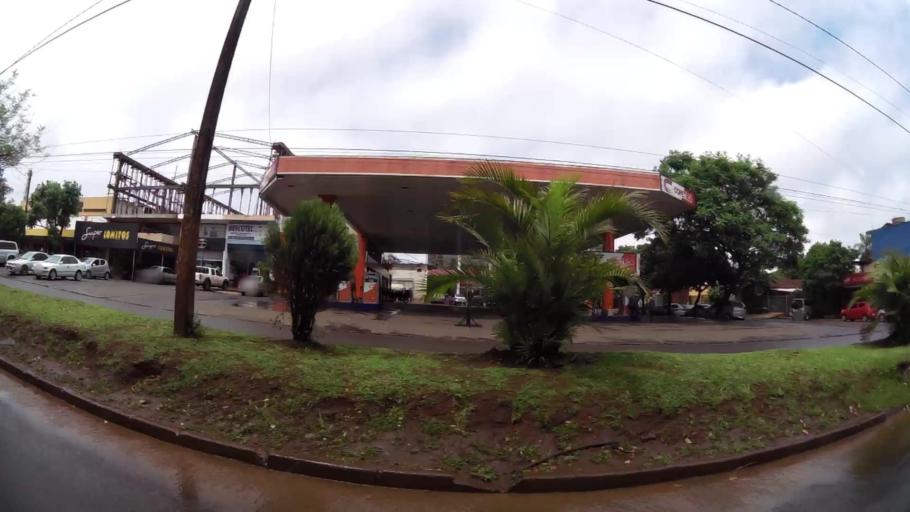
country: PY
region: Alto Parana
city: Presidente Franco
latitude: -25.5122
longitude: -54.6542
